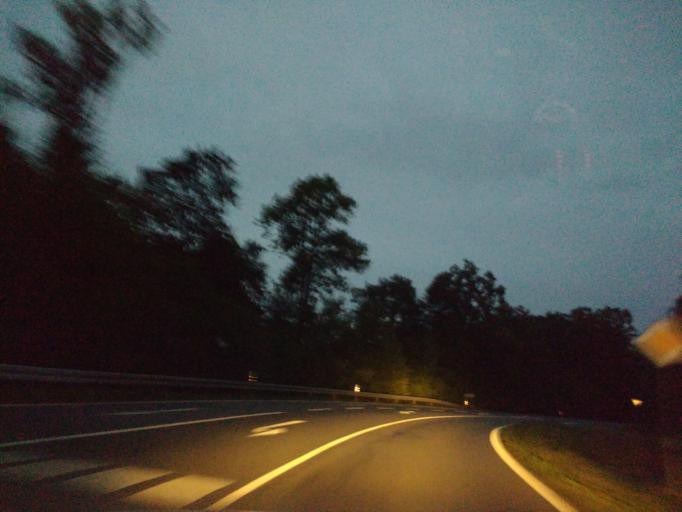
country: DE
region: North Rhine-Westphalia
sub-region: Regierungsbezirk Arnsberg
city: Ruthen
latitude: 51.4689
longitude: 8.3931
